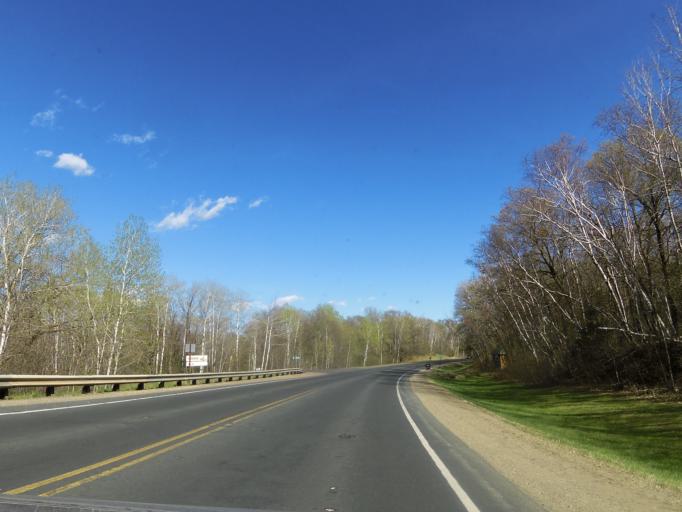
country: US
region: Minnesota
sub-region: Washington County
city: Bayport
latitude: 45.0571
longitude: -92.7292
